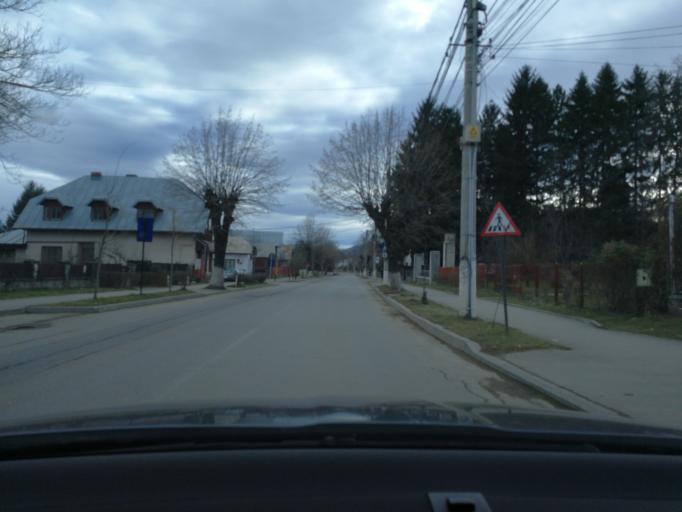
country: RO
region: Prahova
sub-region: Oras Breaza
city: Breaza de Jos
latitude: 45.1751
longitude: 25.6718
